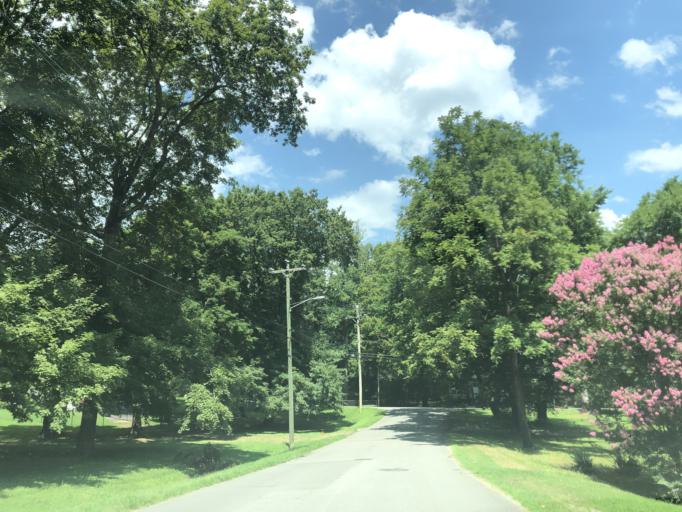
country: US
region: Tennessee
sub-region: Davidson County
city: Lakewood
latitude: 36.1583
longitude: -86.6521
